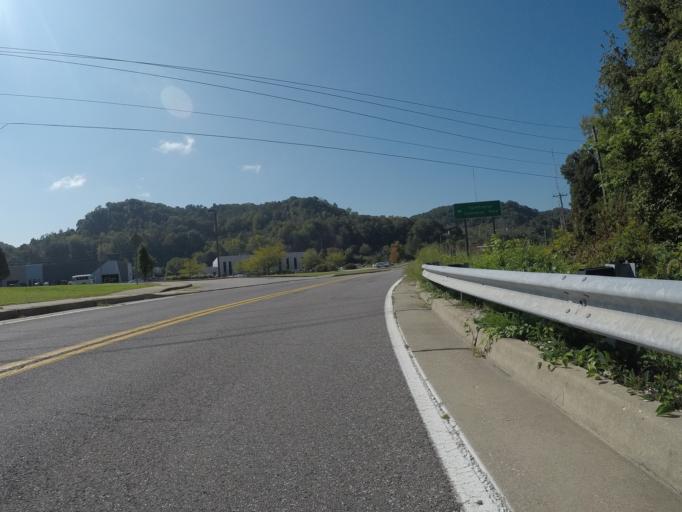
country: US
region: Ohio
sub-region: Lawrence County
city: Burlington
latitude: 38.4036
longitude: -82.4924
